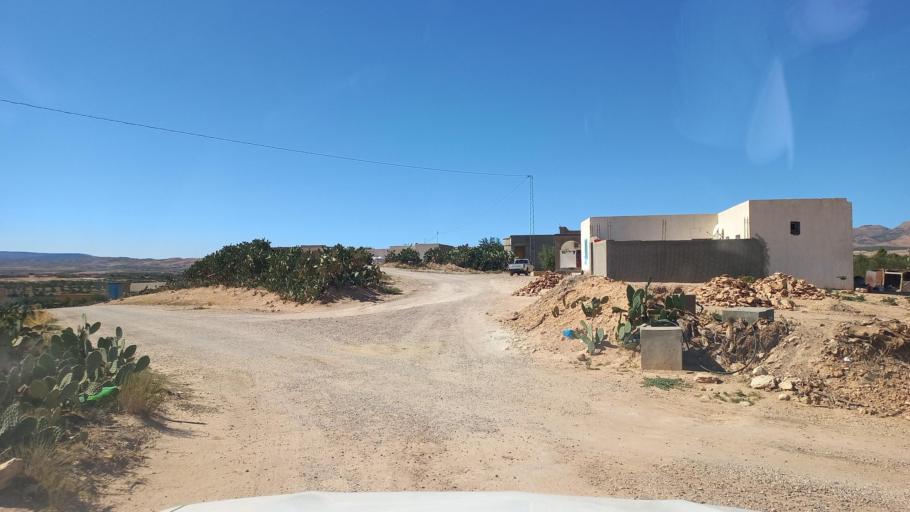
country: TN
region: Al Qasrayn
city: Sbiba
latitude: 35.3784
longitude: 9.0749
